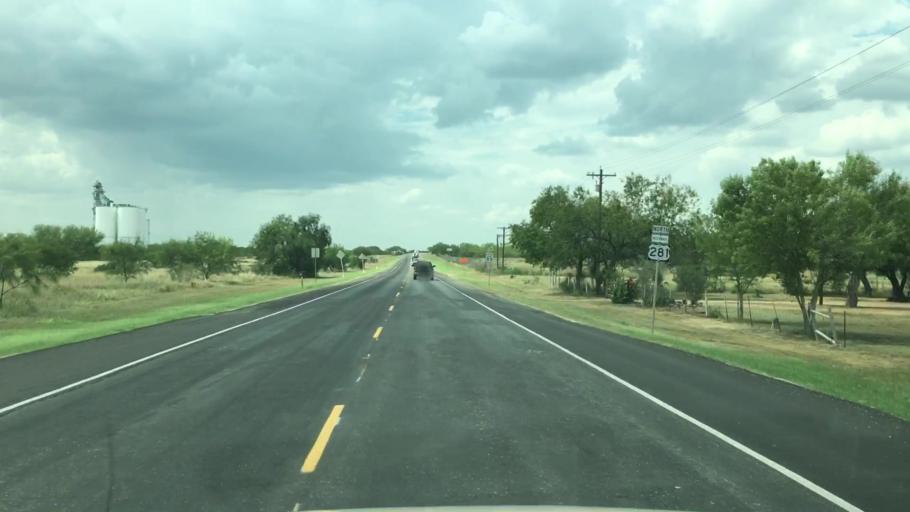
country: US
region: Texas
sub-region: Live Oak County
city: Three Rivers
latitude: 28.6361
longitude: -98.2752
